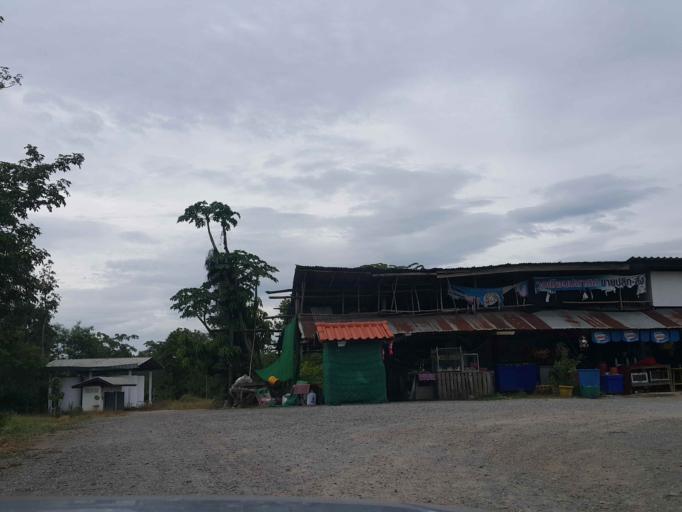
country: TH
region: Sukhothai
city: Thung Saliam
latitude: 17.3497
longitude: 99.4244
